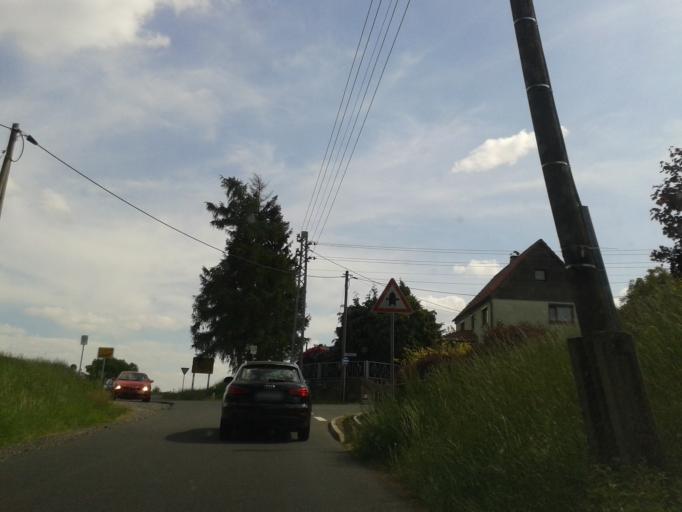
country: DE
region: Saxony
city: Nossen
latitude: 51.0247
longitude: 13.3134
